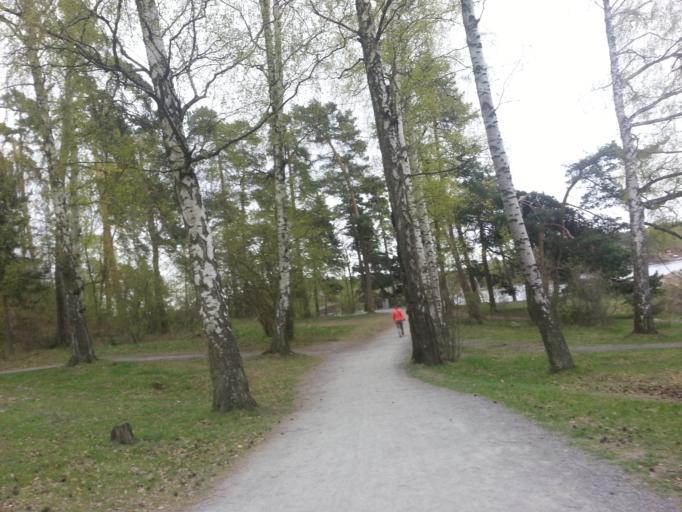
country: NO
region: Akershus
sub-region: Baerum
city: Lysaker
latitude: 59.9127
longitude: 10.6504
